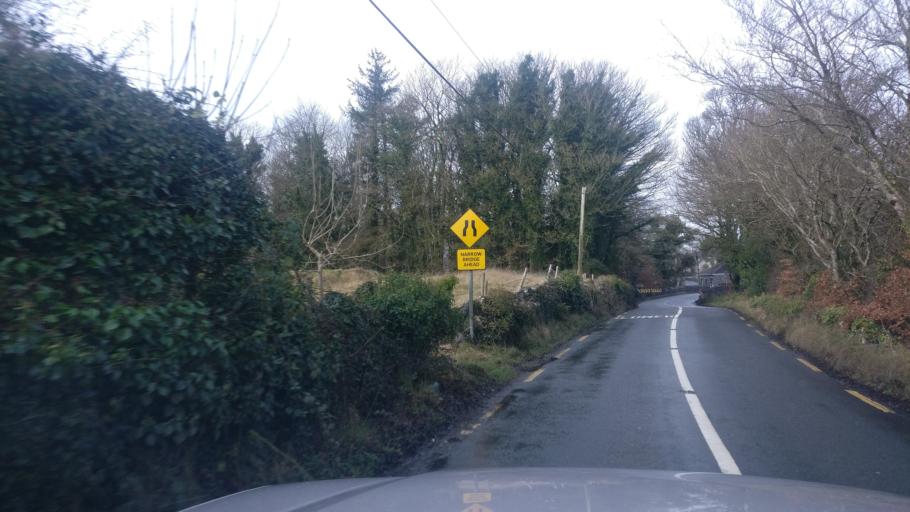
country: IE
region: Connaught
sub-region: County Galway
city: Loughrea
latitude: 53.2836
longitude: -8.5864
